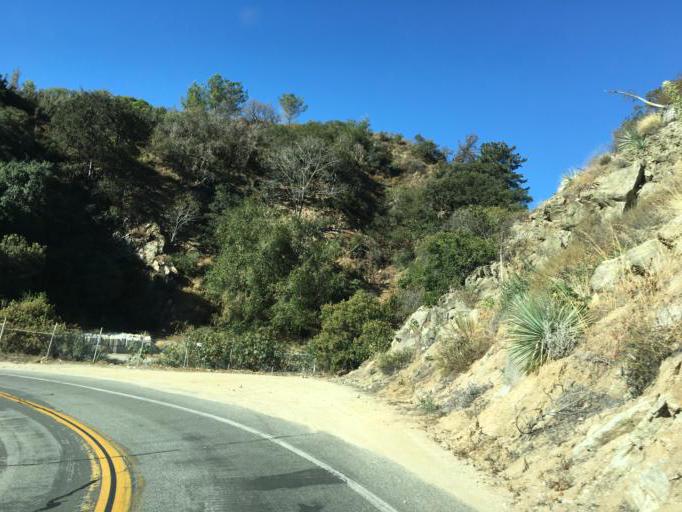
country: US
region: California
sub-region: Los Angeles County
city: Sierra Madre
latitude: 34.1806
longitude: -118.0250
